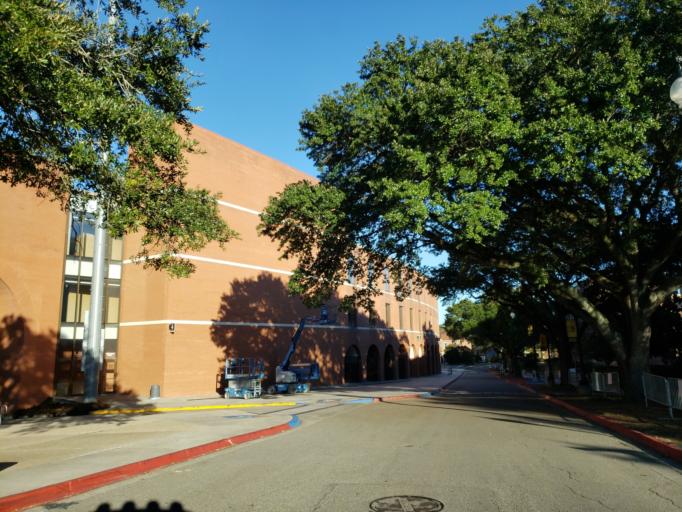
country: US
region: Mississippi
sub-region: Lamar County
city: Arnold Line
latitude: 31.3281
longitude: -89.3322
